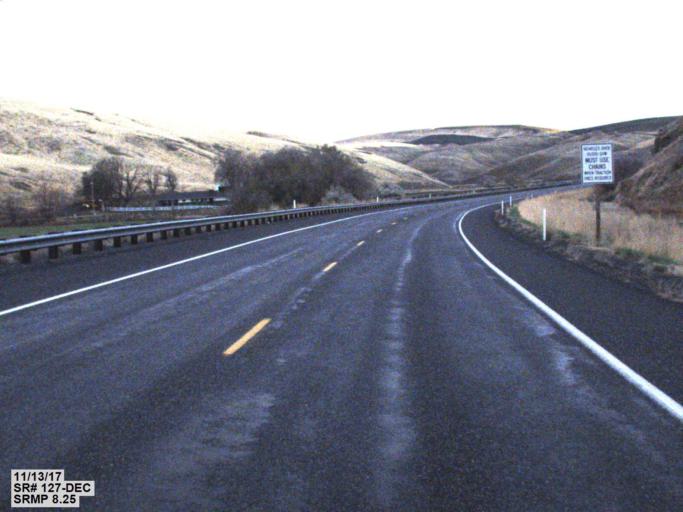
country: US
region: Washington
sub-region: Garfield County
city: Pomeroy
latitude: 46.6052
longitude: -117.7854
